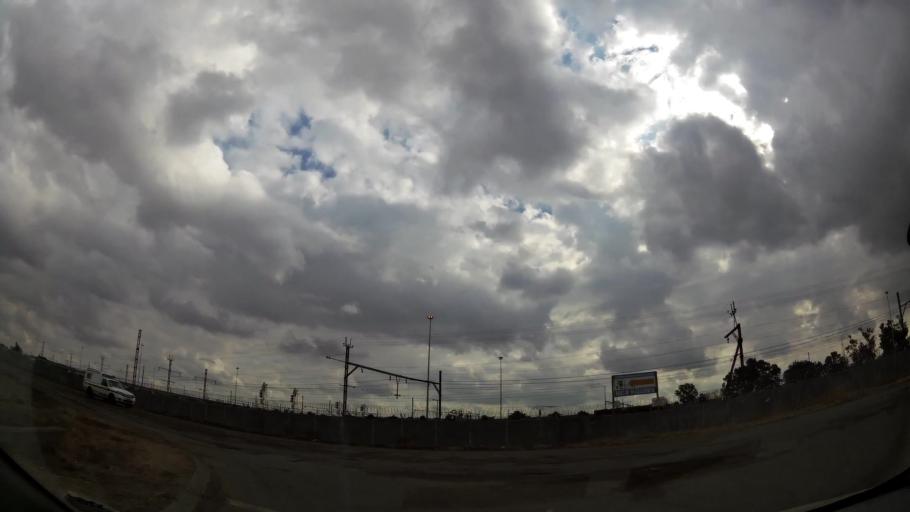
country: ZA
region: Orange Free State
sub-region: Fezile Dabi District Municipality
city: Sasolburg
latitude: -26.8524
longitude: 27.8686
